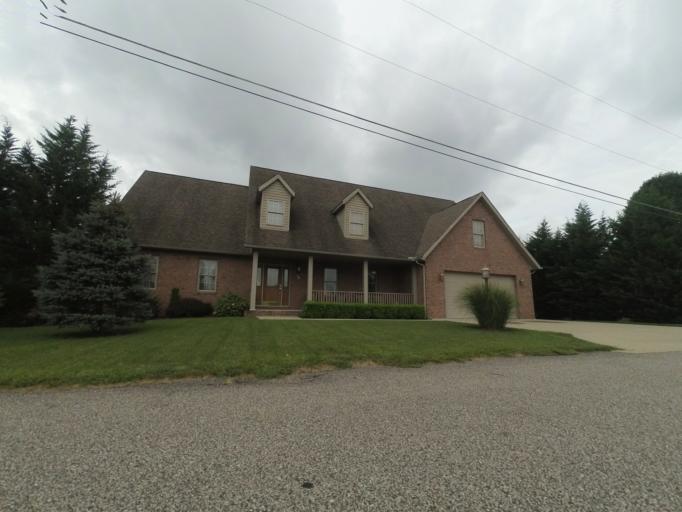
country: US
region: West Virginia
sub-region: Cabell County
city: Huntington
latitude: 38.4320
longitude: -82.4717
